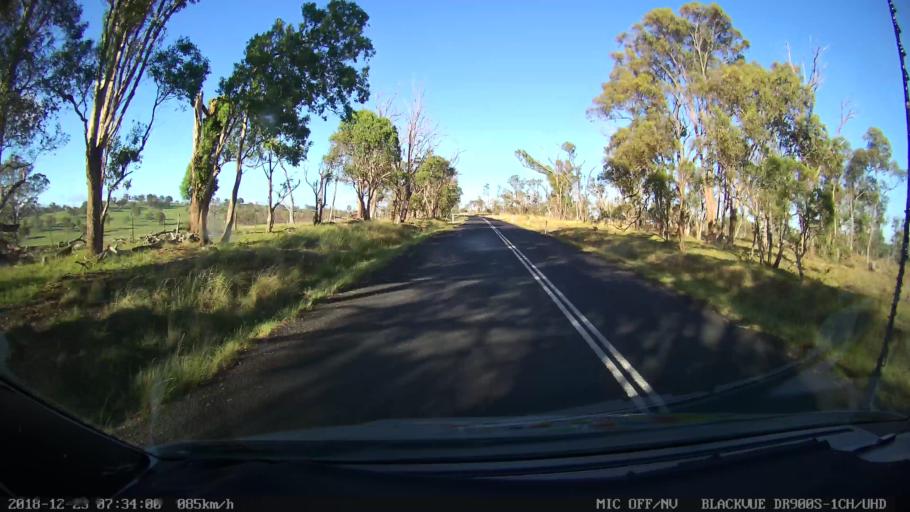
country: AU
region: New South Wales
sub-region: Armidale Dumaresq
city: Enmore
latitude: -30.5174
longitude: 152.0981
